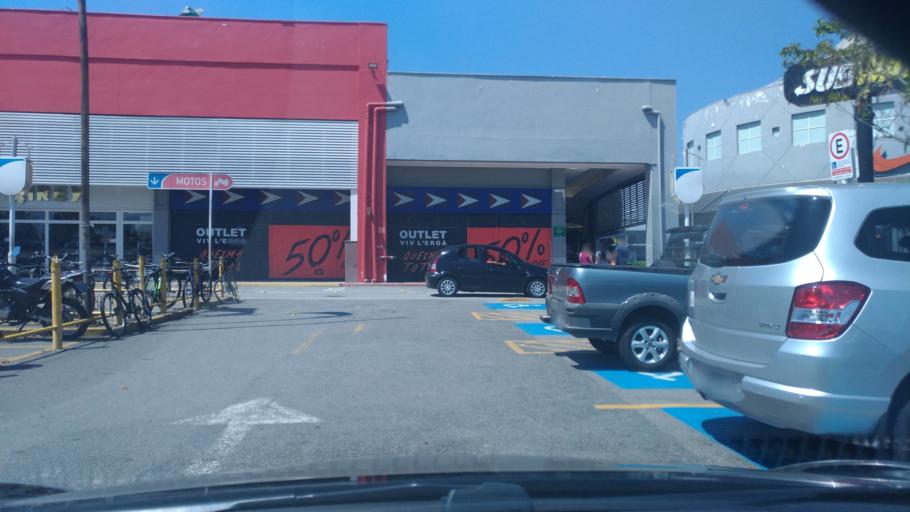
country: BR
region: Sao Paulo
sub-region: Sao Bernardo Do Campo
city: Sao Bernardo do Campo
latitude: -23.6685
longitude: -46.5748
